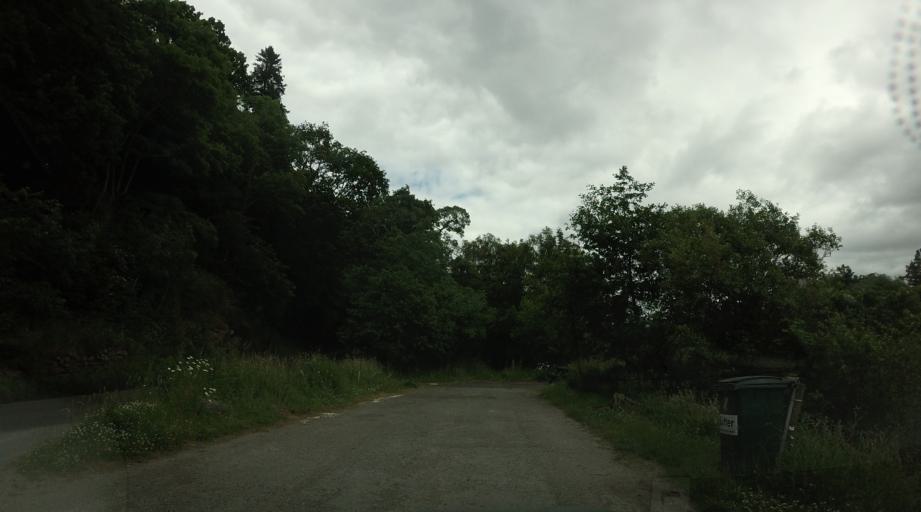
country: GB
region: Scotland
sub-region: Perth and Kinross
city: Aberfeldy
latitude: 56.7017
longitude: -4.1748
